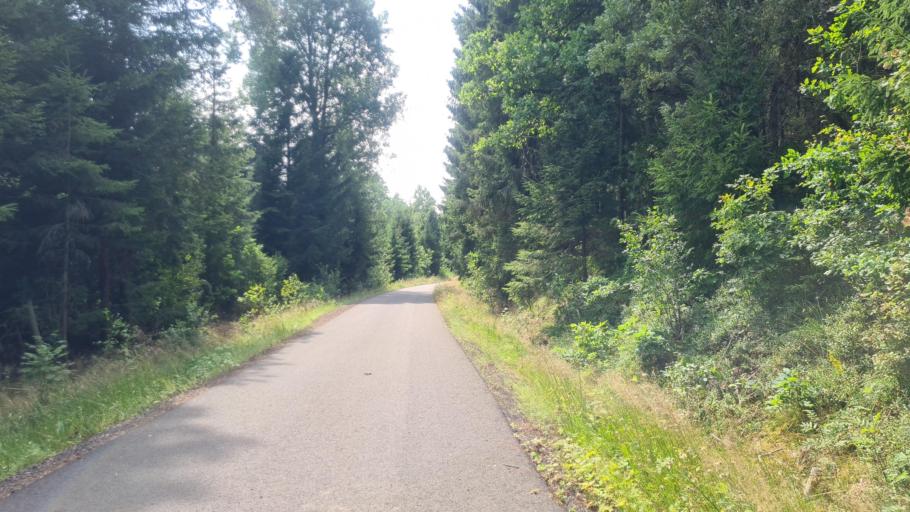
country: SE
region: Kronoberg
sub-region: Ljungby Kommun
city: Ljungby
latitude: 56.8611
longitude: 13.9777
